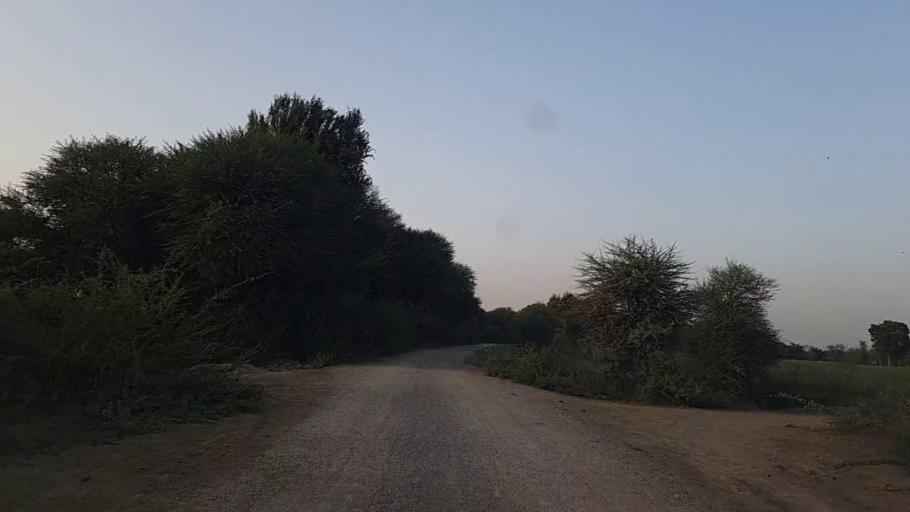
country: PK
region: Sindh
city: Naukot
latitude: 24.6995
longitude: 69.2732
